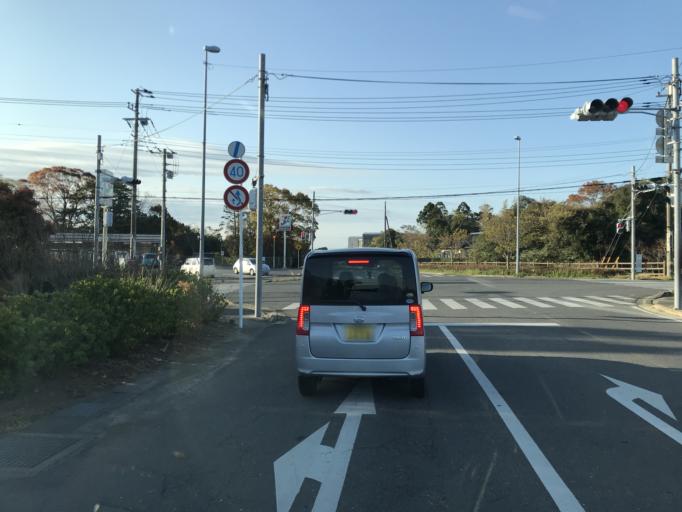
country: JP
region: Chiba
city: Yokaichiba
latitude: 35.6910
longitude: 140.5690
